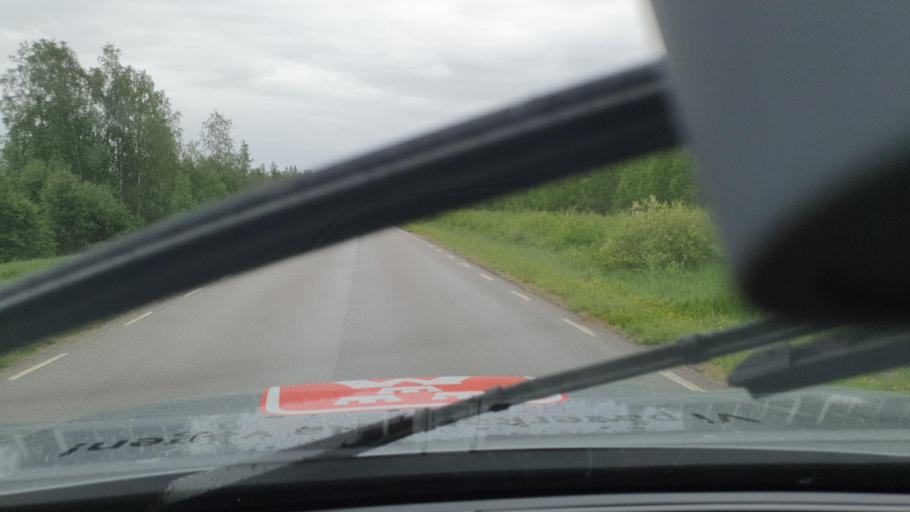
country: SE
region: Norrbotten
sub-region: Pajala Kommun
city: Pajala
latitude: 66.7924
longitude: 23.1255
